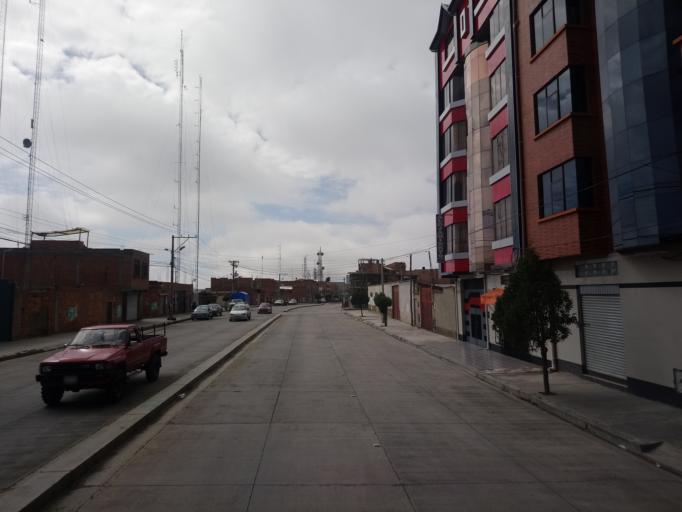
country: BO
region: La Paz
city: La Paz
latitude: -16.5153
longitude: -68.1516
